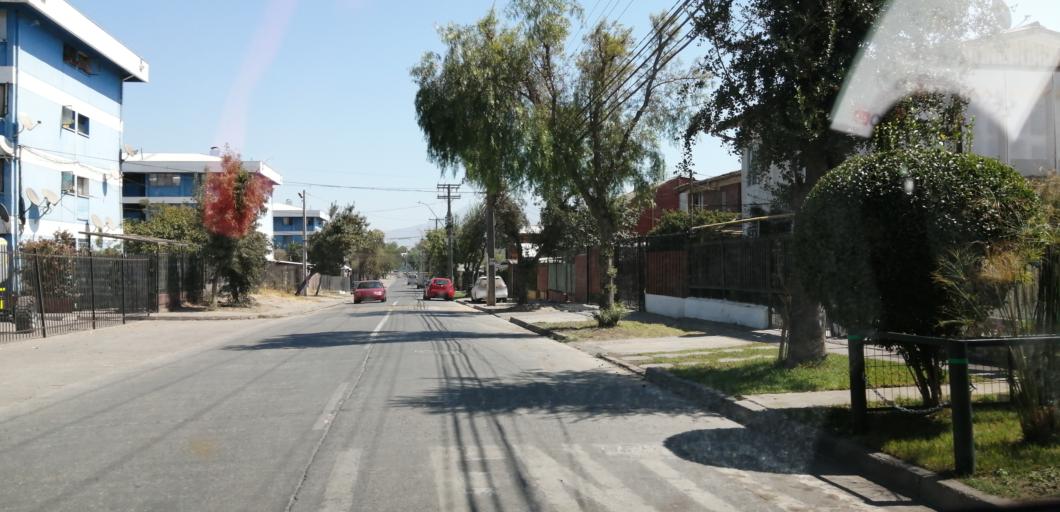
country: CL
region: Santiago Metropolitan
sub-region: Provincia de Santiago
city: Lo Prado
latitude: -33.4462
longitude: -70.7473
